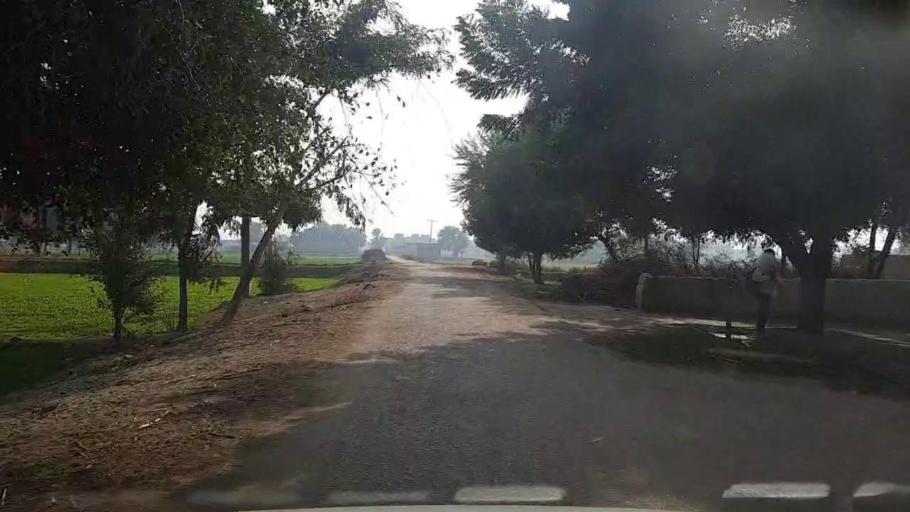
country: PK
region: Sindh
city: Setharja Old
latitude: 27.1224
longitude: 68.5159
